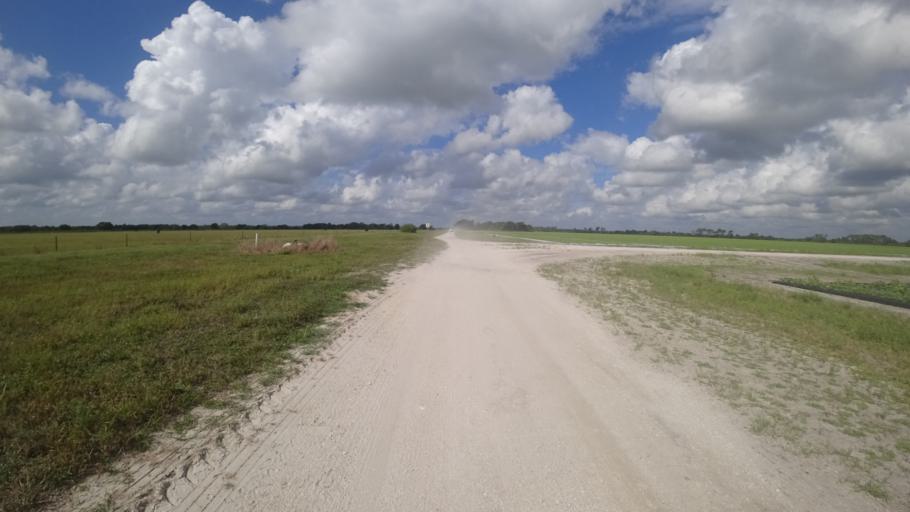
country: US
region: Florida
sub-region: Sarasota County
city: Lake Sarasota
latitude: 27.4034
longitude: -82.2116
